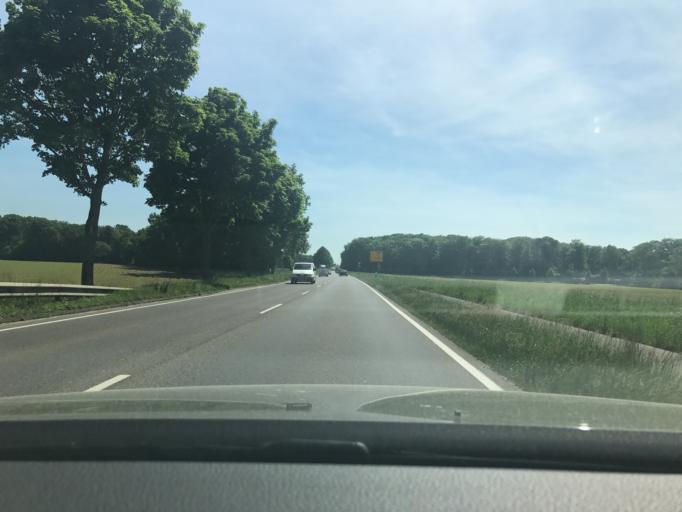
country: DE
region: North Rhine-Westphalia
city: Tonisvorst
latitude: 51.3042
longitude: 6.4776
